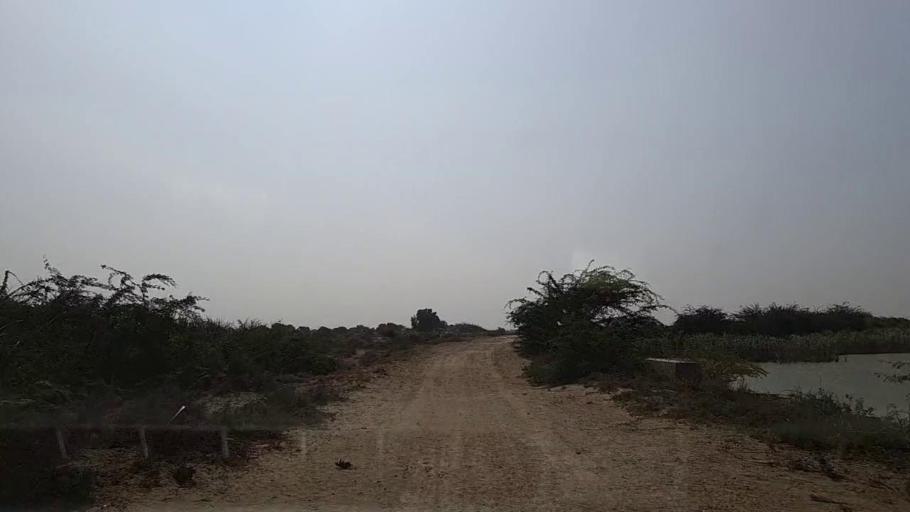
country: PK
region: Sindh
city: Mirpur Sakro
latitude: 24.5464
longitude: 67.7899
